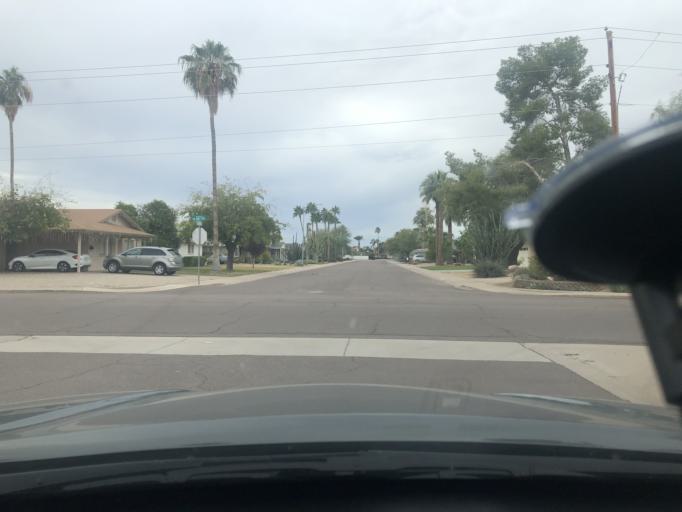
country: US
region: Arizona
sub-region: Maricopa County
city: Scottsdale
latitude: 33.4908
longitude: -111.8959
